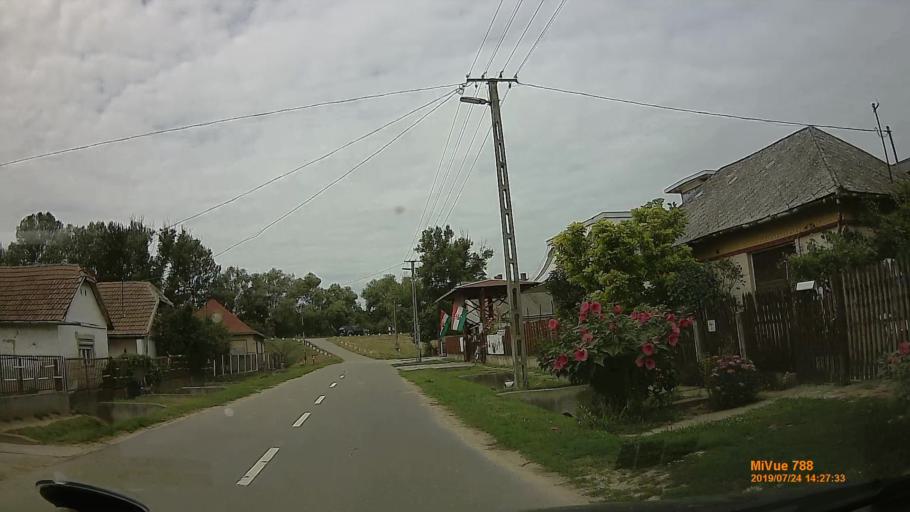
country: HU
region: Szabolcs-Szatmar-Bereg
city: Mandok
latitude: 48.3333
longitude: 22.2636
